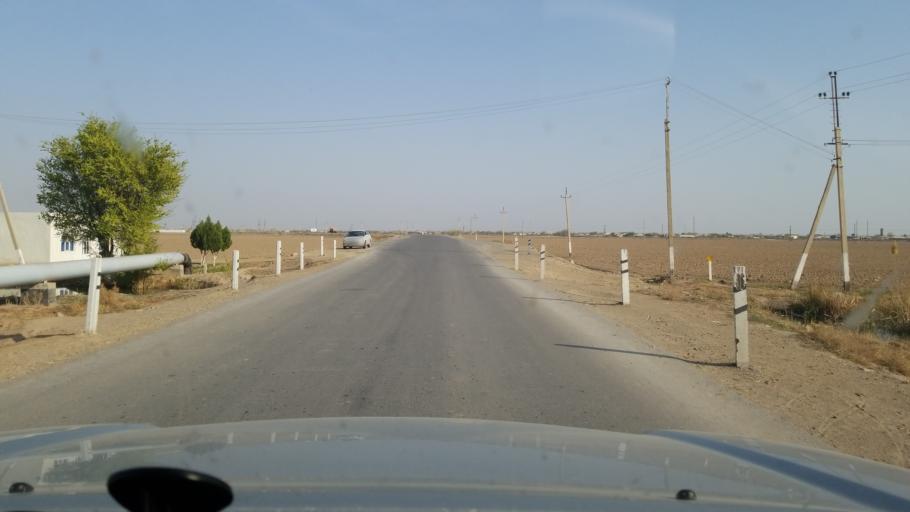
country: AF
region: Jowzjan
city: Khamyab
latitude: 37.6082
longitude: 65.7310
